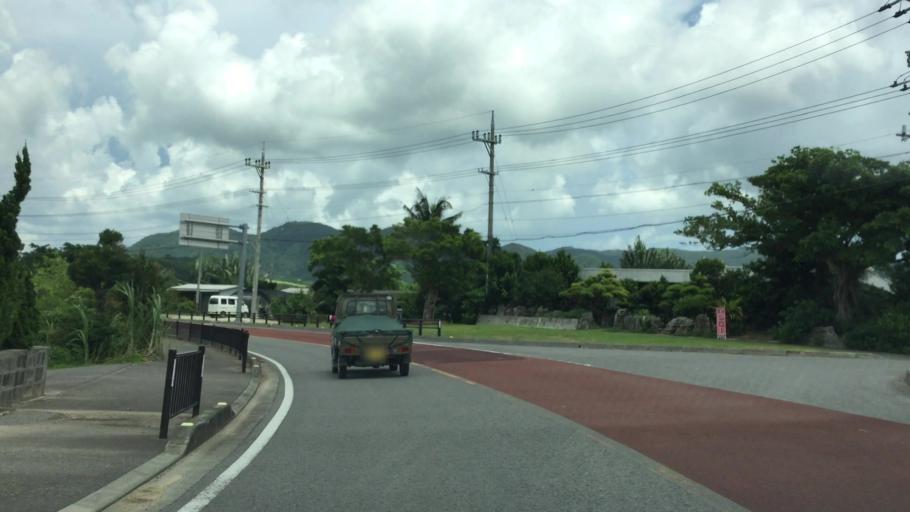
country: JP
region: Okinawa
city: Ishigaki
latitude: 24.3963
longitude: 124.1563
